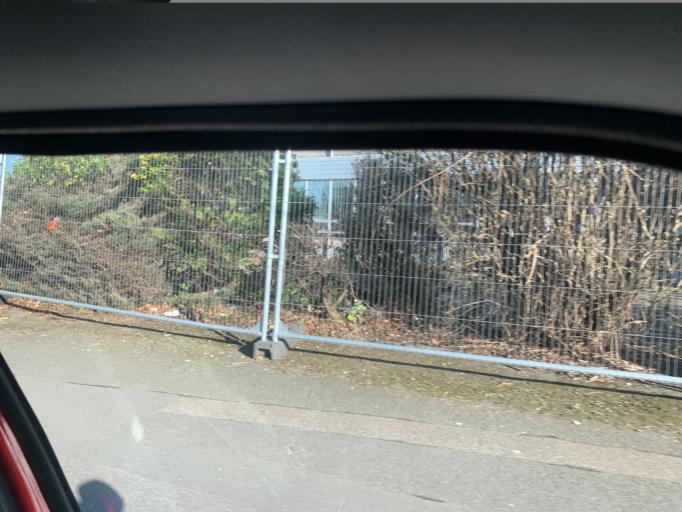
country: GB
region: England
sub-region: Buckinghamshire
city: Farnham Royal
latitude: 51.5167
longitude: -0.6246
